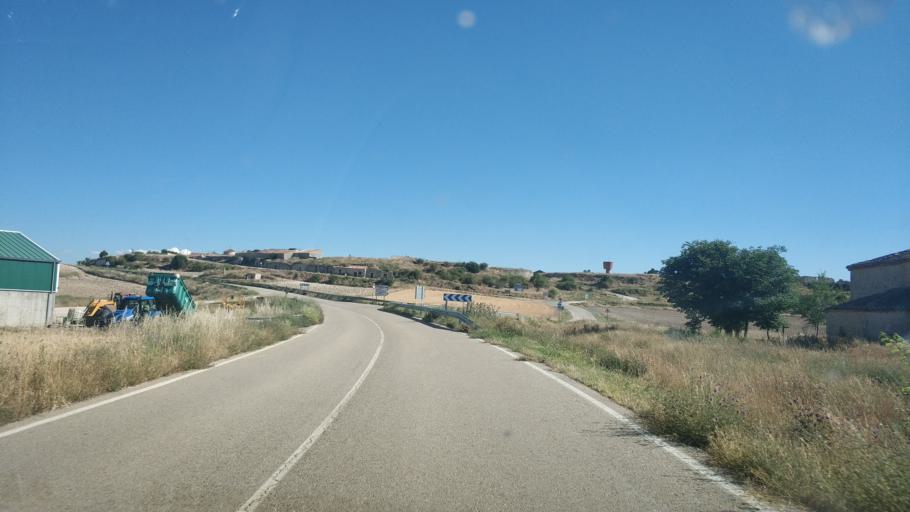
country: ES
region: Castille and Leon
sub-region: Provincia de Soria
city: Liceras
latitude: 41.4681
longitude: -3.2174
